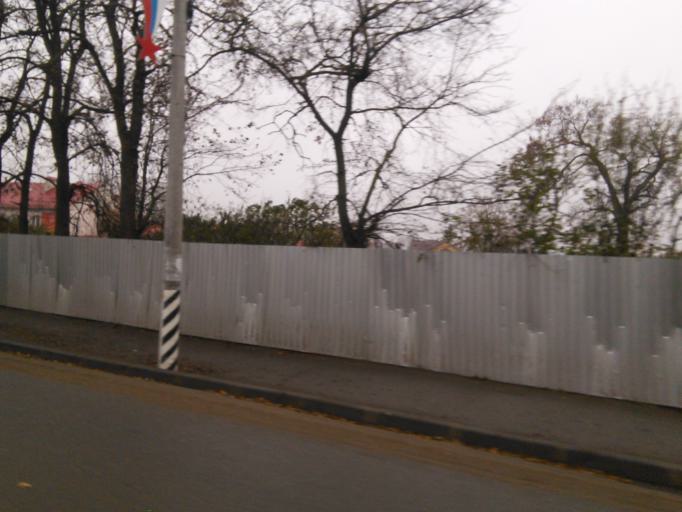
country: RU
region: Jaroslavl
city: Pereslavl'-Zalesskiy
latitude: 56.7442
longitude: 38.8569
